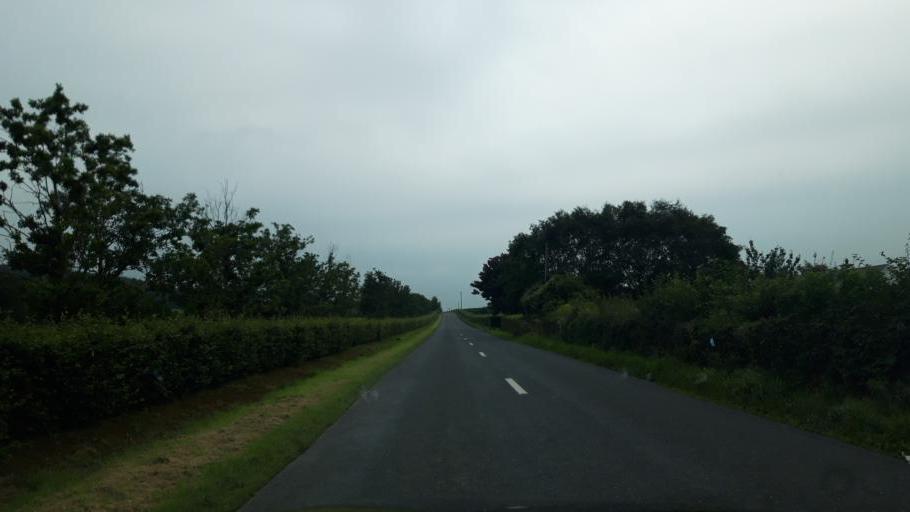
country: IE
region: Munster
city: Fethard
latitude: 52.4897
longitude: -7.6915
